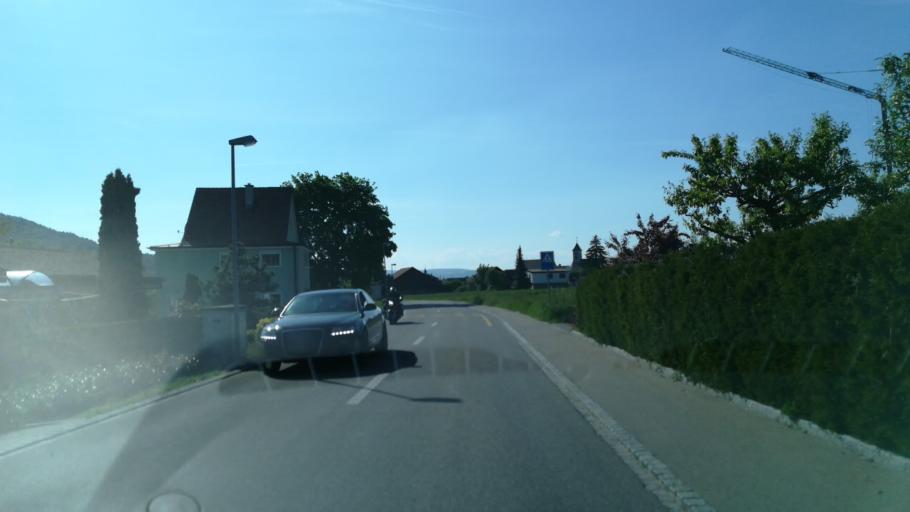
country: CH
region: Schaffhausen
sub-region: Bezirk Stein
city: Ramsen
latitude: 47.7052
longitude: 8.8161
